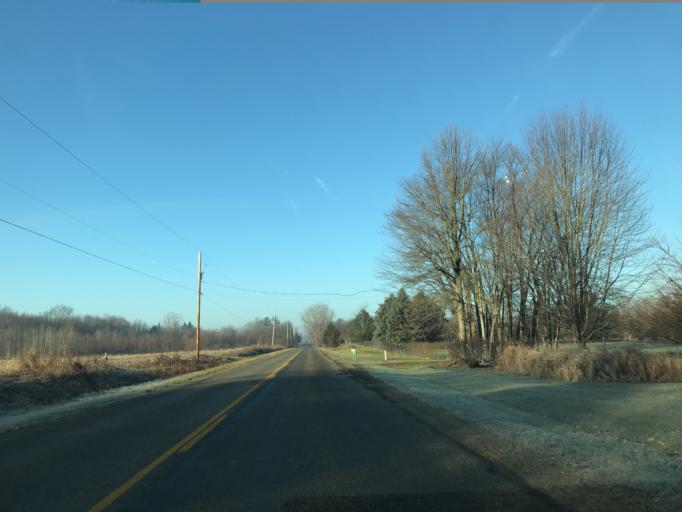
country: US
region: Michigan
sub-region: Eaton County
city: Dimondale
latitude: 42.6621
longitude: -84.6137
